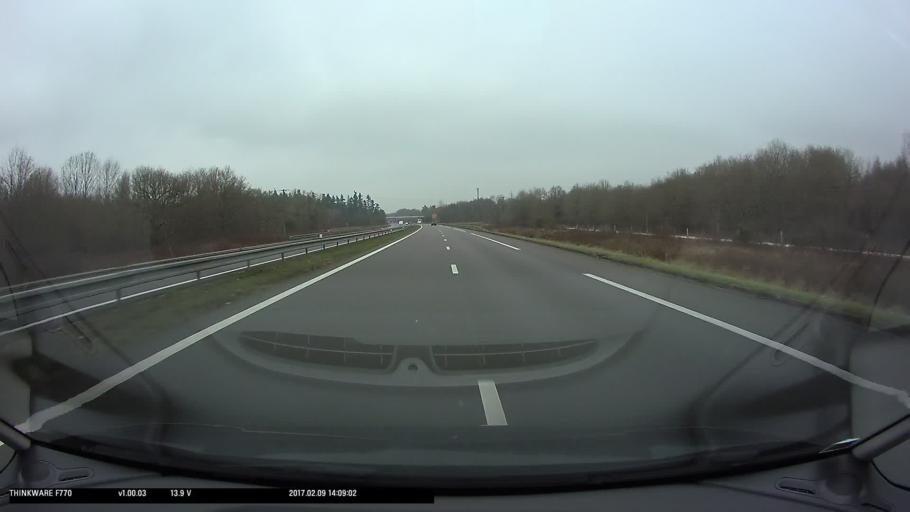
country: FR
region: Centre
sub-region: Departement du Loir-et-Cher
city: Salbris
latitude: 47.4550
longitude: 2.0043
